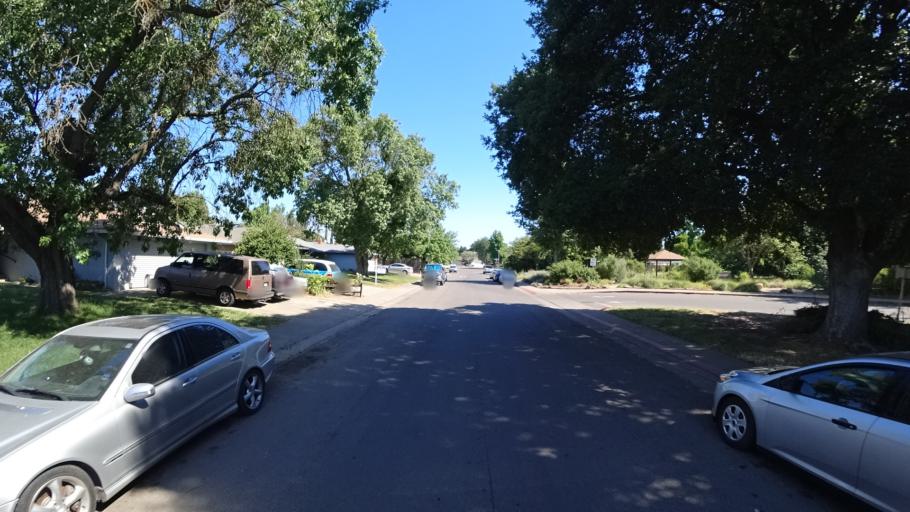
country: US
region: California
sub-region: Sacramento County
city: Rosemont
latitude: 38.5536
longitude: -121.3875
